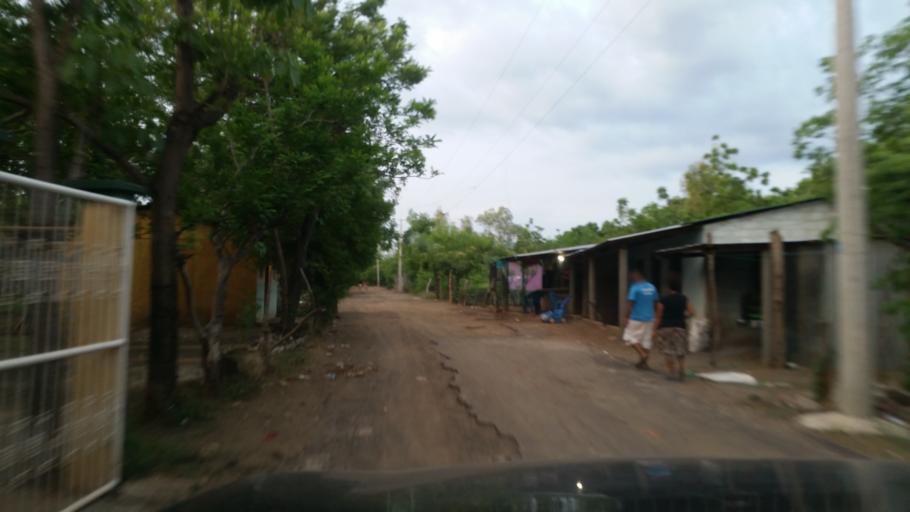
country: NI
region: Managua
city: Masachapa
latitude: 11.7718
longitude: -86.5021
